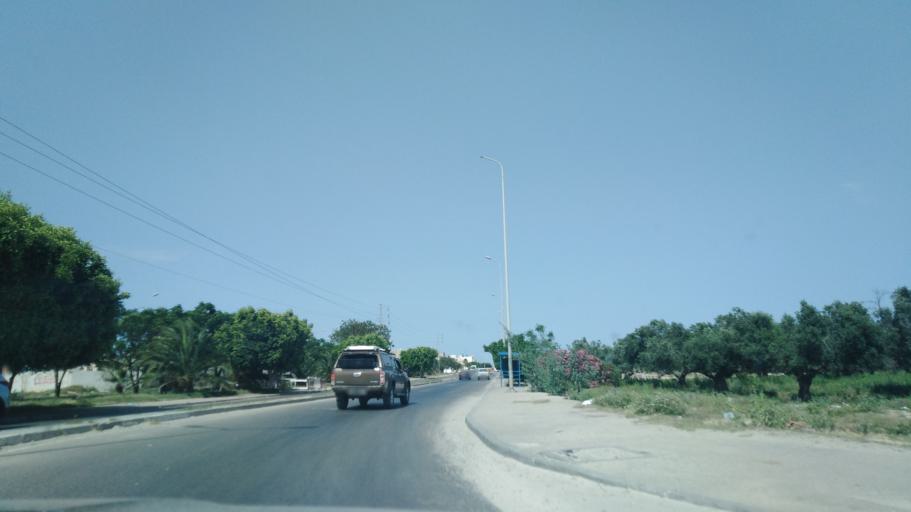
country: TN
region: Susah
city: Sousse
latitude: 35.7931
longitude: 10.5959
